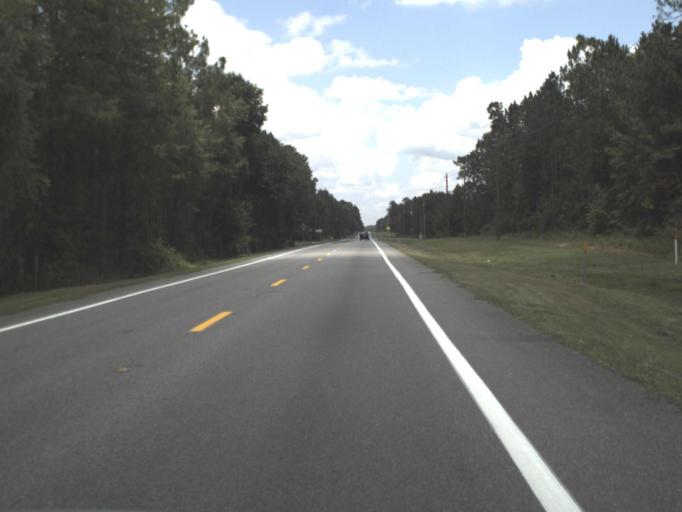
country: US
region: Florida
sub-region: Union County
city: Lake Butler
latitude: 30.0283
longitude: -82.3197
